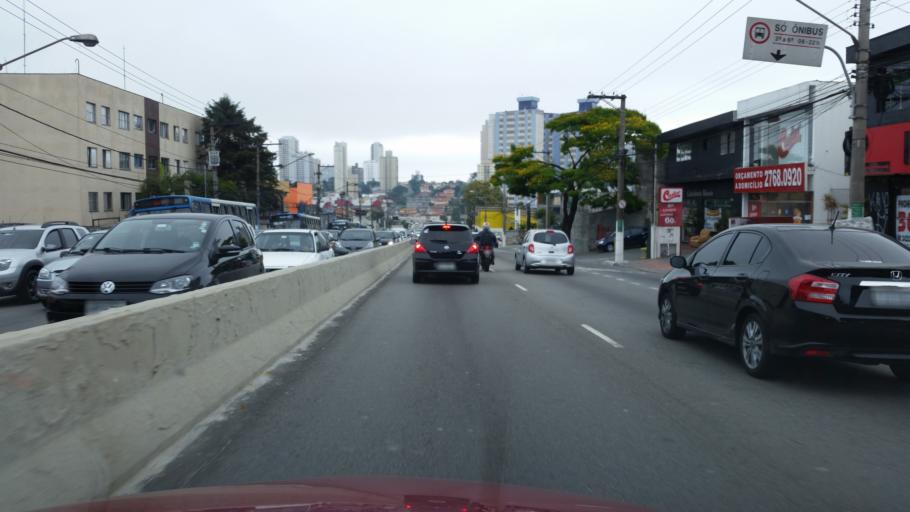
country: BR
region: Sao Paulo
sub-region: Diadema
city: Diadema
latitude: -23.6486
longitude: -46.6761
